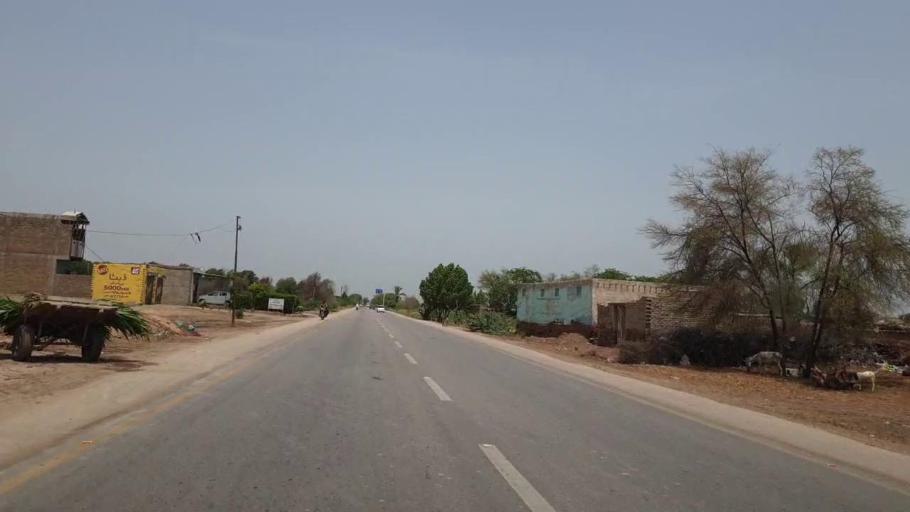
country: PK
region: Sindh
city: Nawabshah
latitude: 26.2380
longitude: 68.4744
